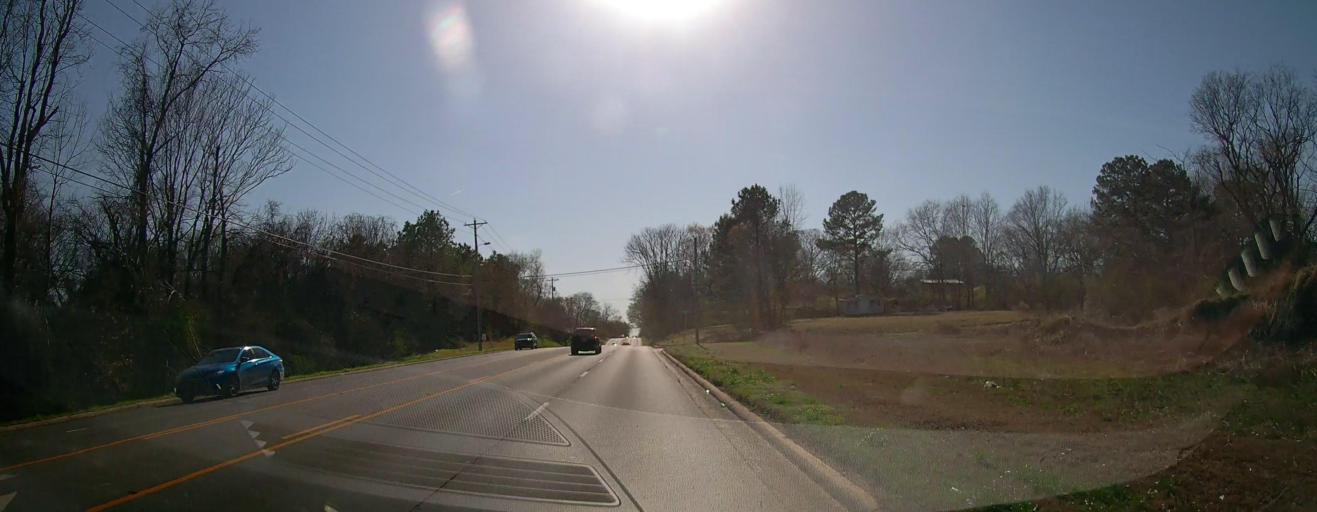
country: US
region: Alabama
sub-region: Lauderdale County
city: East Florence
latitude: 34.8101
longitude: -87.6353
